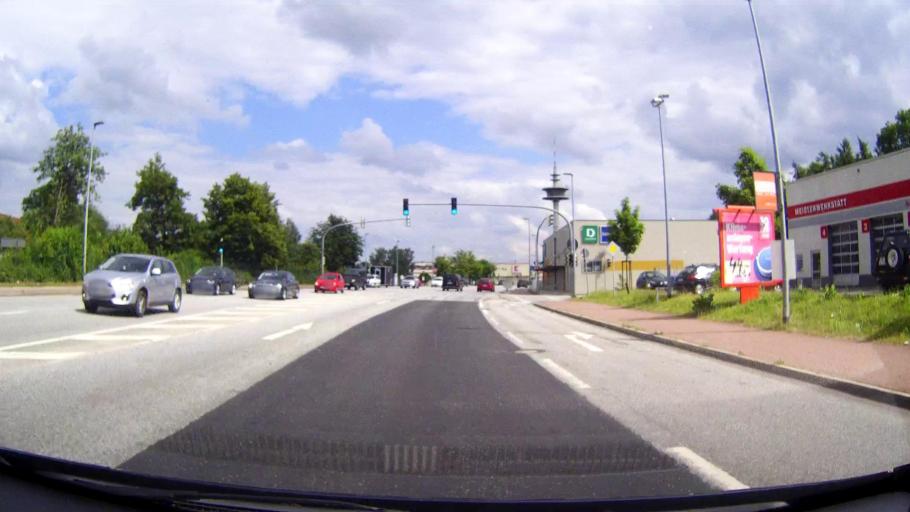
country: DE
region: Schleswig-Holstein
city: Bad Segeberg
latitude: 53.9349
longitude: 10.3067
